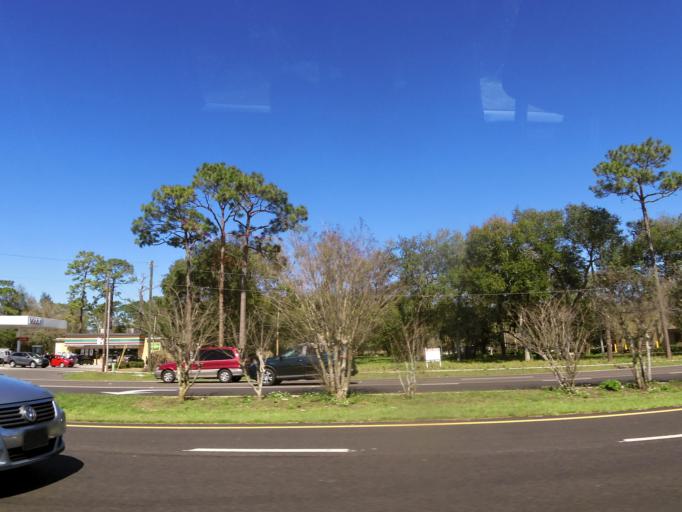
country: US
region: Florida
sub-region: Orange County
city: Apopka
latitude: 28.6859
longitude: -81.5353
